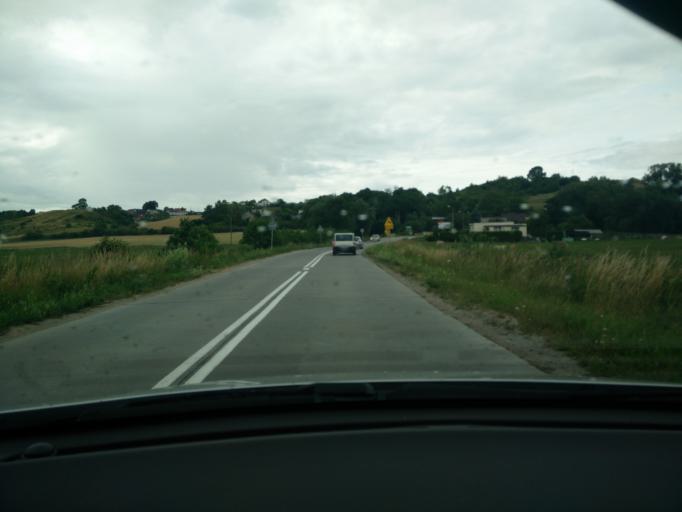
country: PL
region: Pomeranian Voivodeship
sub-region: Powiat pucki
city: Mrzezino
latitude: 54.6462
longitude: 18.4361
